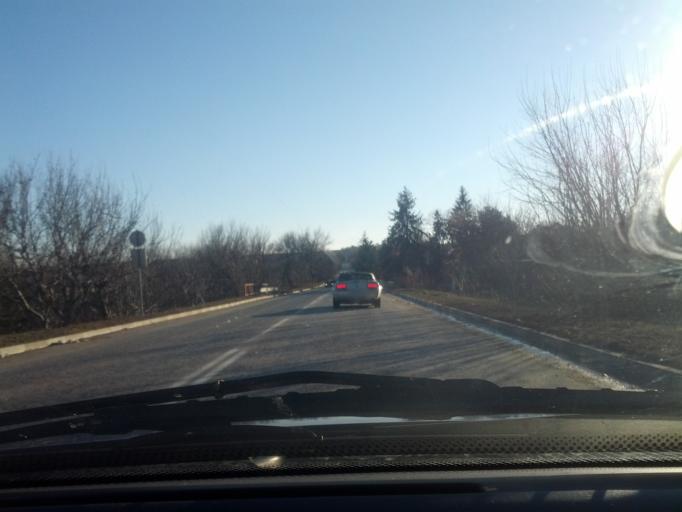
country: BG
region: Vratsa
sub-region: Obshtina Miziya
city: Miziya
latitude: 43.5911
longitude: 23.8185
